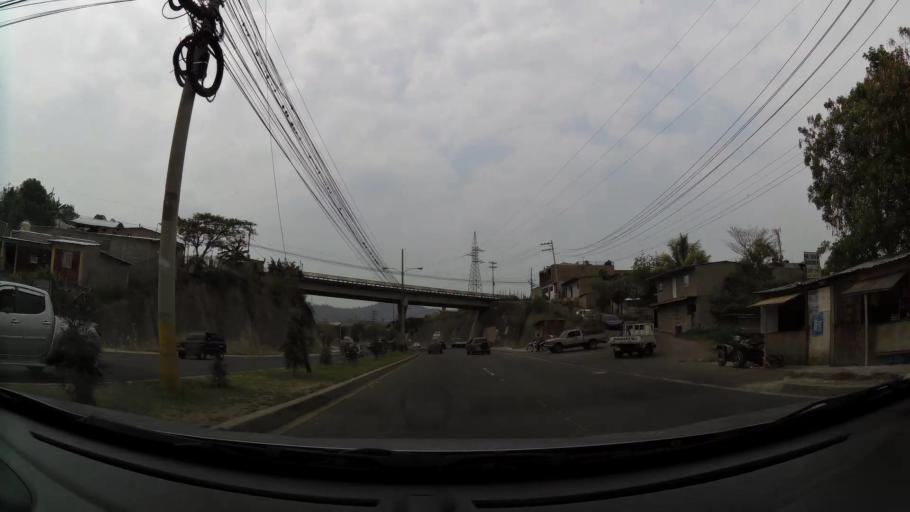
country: HN
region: Francisco Morazan
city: Yaguacire
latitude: 14.0535
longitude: -87.2537
